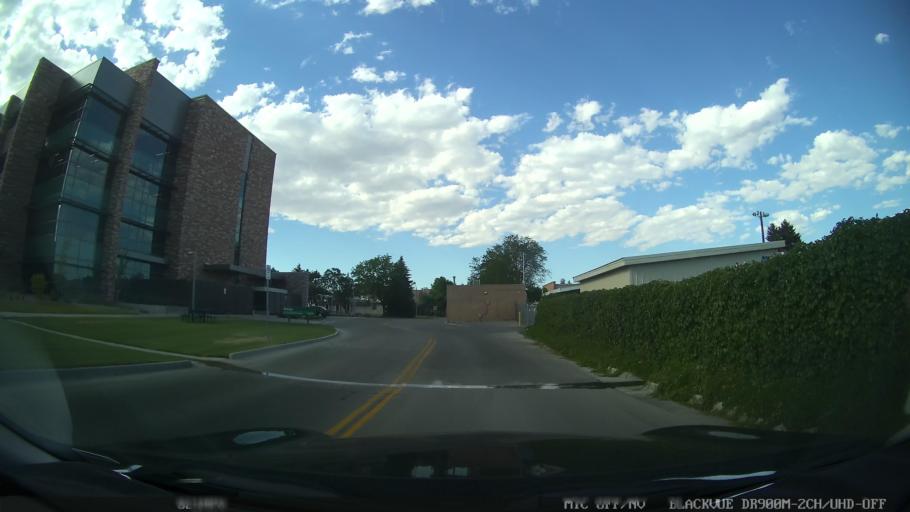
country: US
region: Colorado
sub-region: Larimer County
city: Fort Collins
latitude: 40.5700
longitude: -105.0807
